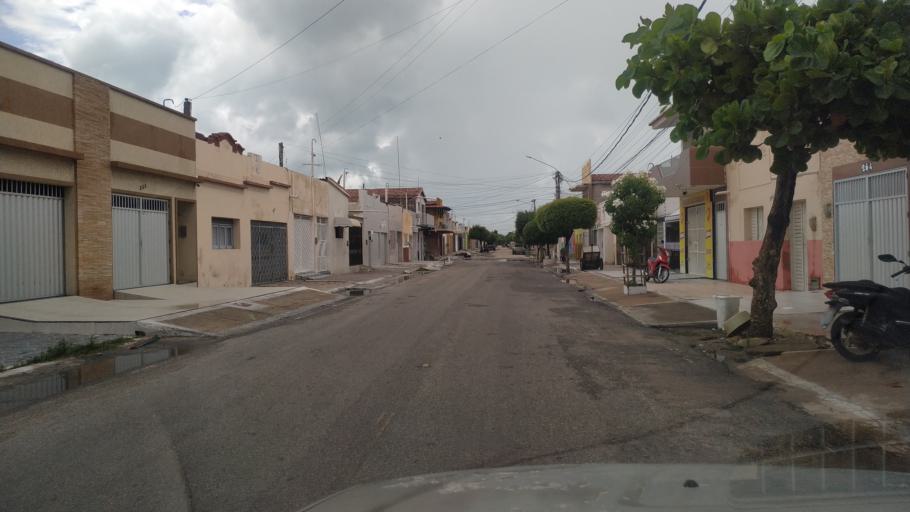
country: BR
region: Rio Grande do Norte
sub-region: Areia Branca
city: Areia Branca
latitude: -4.9539
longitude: -37.1353
